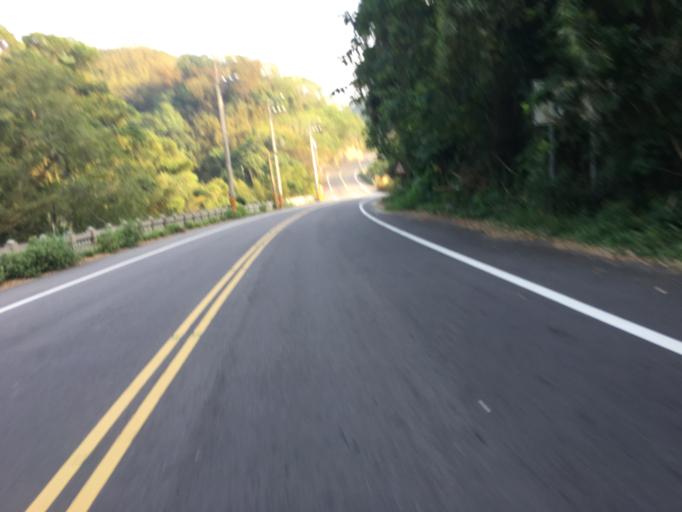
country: TW
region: Taiwan
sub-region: Hsinchu
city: Hsinchu
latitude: 24.7307
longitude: 121.0304
